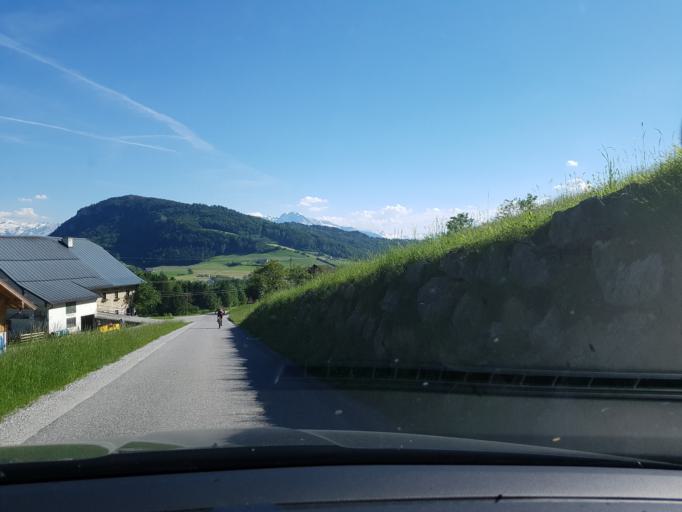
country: AT
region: Salzburg
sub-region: Politischer Bezirk Salzburg-Umgebung
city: Koppl
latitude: 47.7829
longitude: 13.1233
